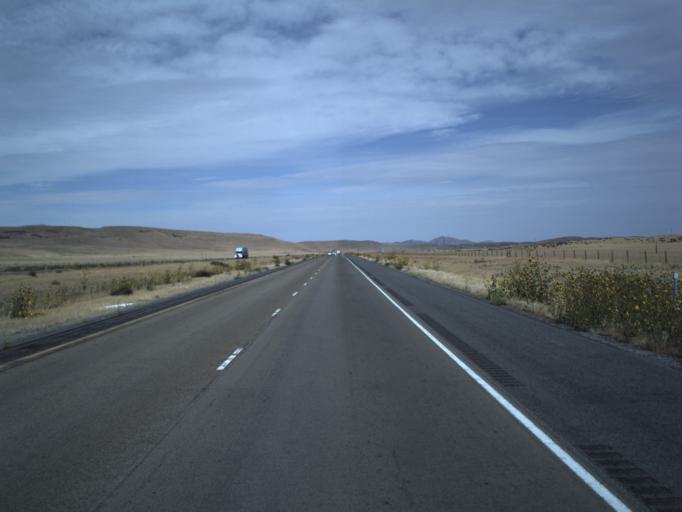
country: US
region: Utah
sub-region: Tooele County
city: Grantsville
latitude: 40.7917
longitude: -112.8339
